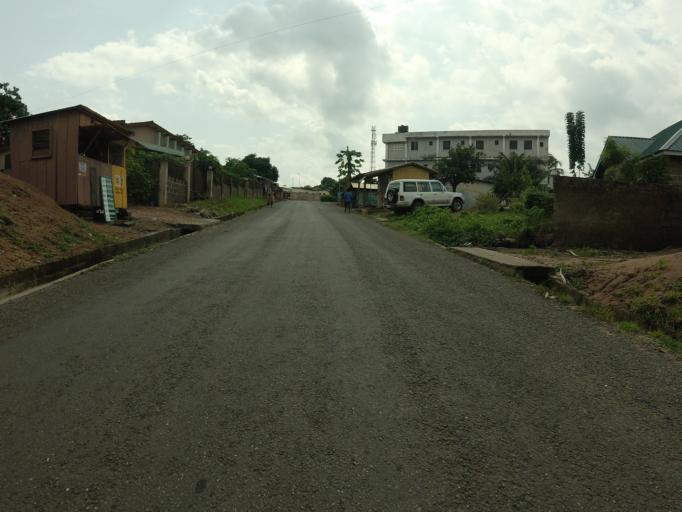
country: GH
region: Volta
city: Ho
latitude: 6.6182
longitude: 0.4753
